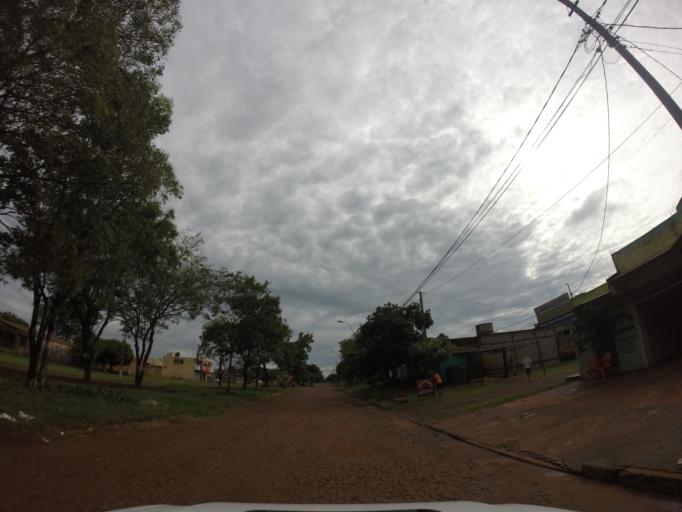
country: PY
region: Alto Parana
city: Ciudad del Este
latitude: -25.3909
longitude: -54.6436
